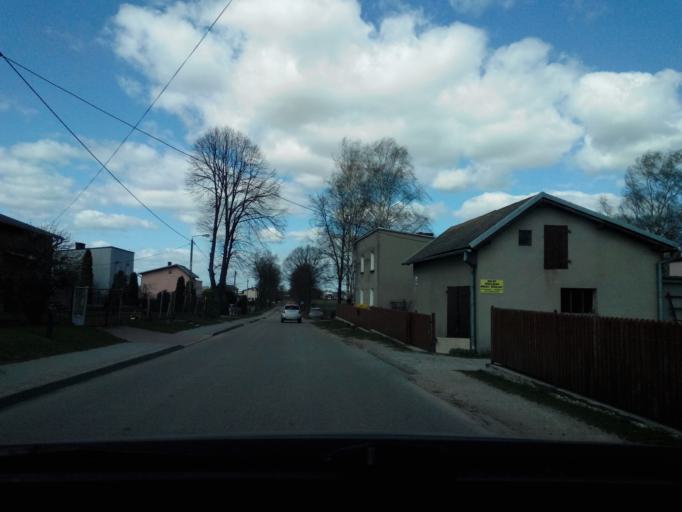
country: PL
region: Warmian-Masurian Voivodeship
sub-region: Powiat nowomiejski
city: Biskupiec
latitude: 53.4714
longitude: 19.3195
